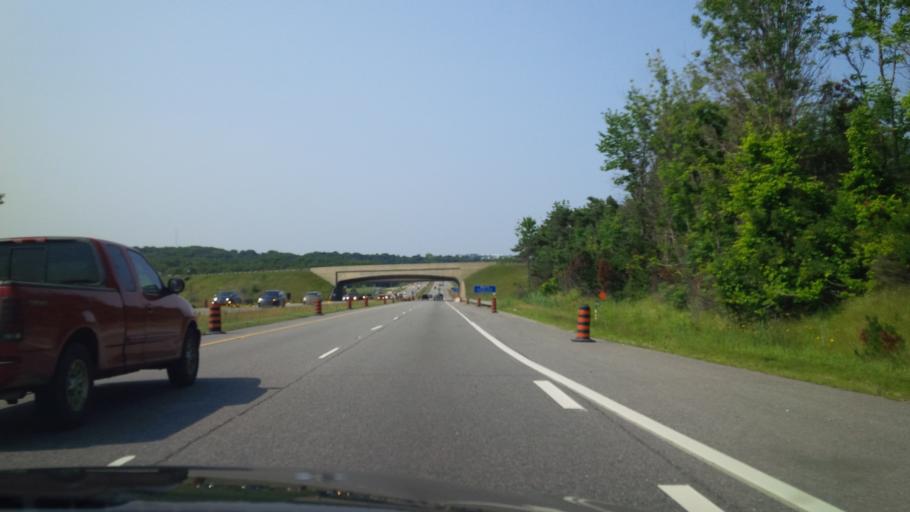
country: CA
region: Ontario
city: Barrie
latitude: 44.4307
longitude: -79.6491
